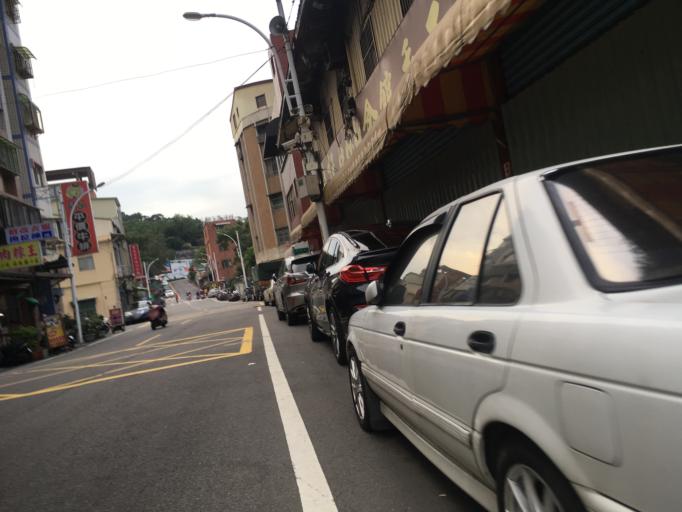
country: TW
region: Taiwan
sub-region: Taoyuan
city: Taoyuan
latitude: 24.9309
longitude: 121.3693
